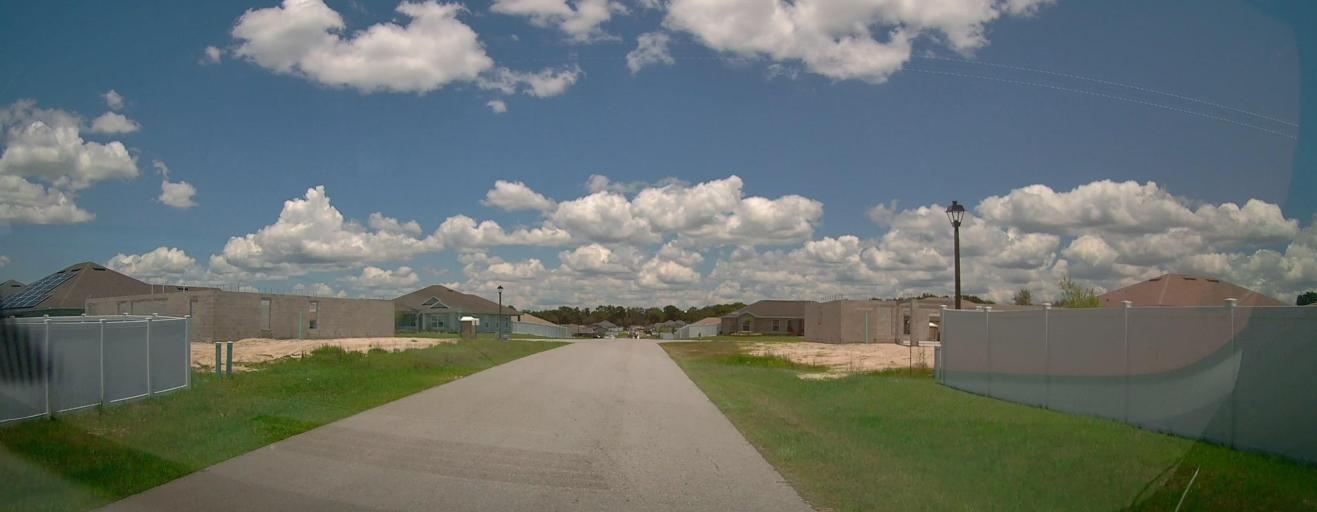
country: US
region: Florida
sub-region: Marion County
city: Belleview
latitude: 29.0874
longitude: -82.0634
